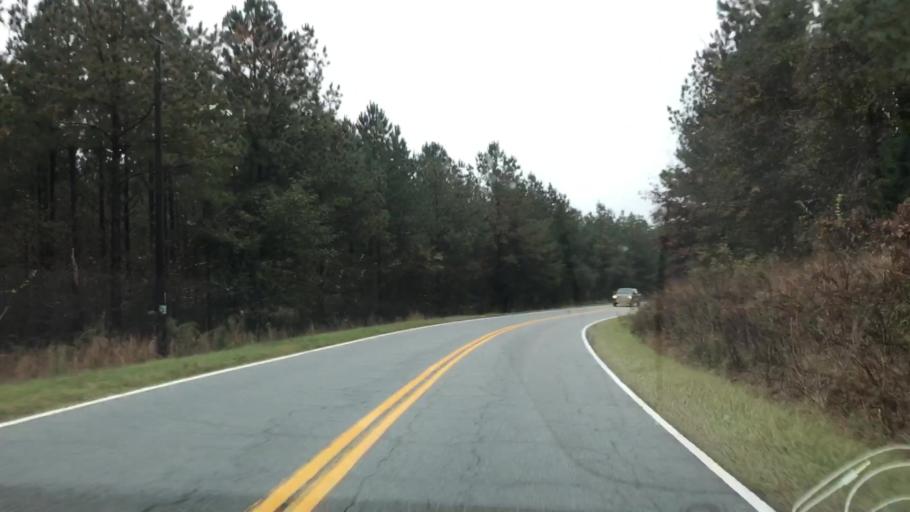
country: US
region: South Carolina
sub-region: Laurens County
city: Joanna
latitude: 34.3686
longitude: -81.7805
